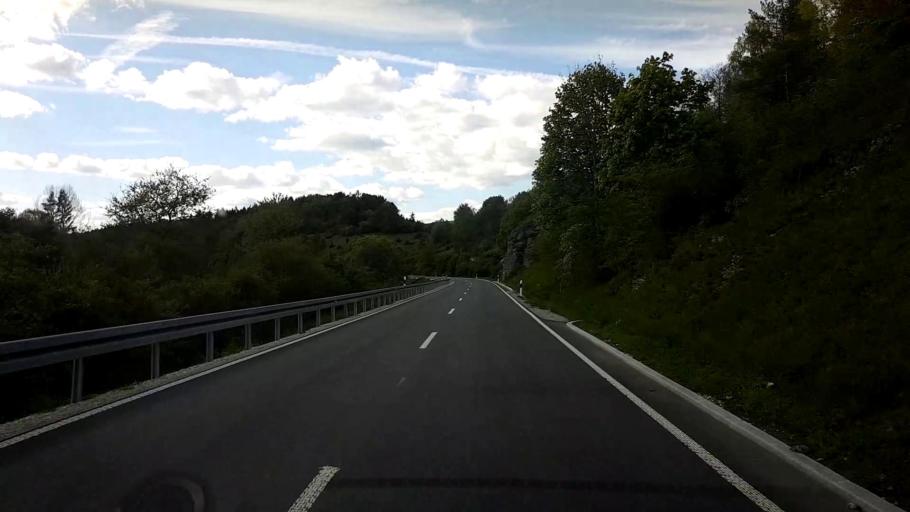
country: DE
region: Bavaria
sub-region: Upper Franconia
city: Hollfeld
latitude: 49.9505
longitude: 11.2783
